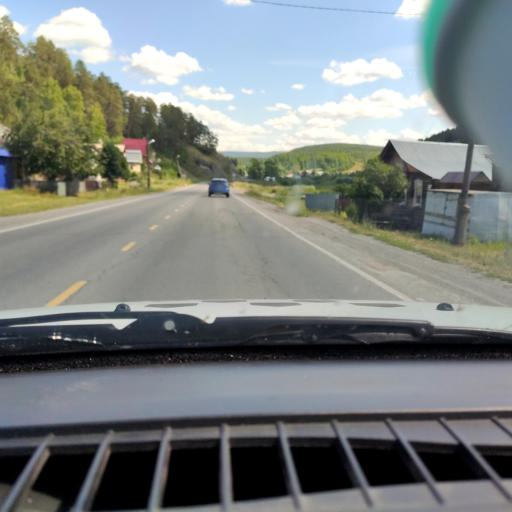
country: RU
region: Chelyabinsk
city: Mezhevoy
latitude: 55.1607
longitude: 58.8068
